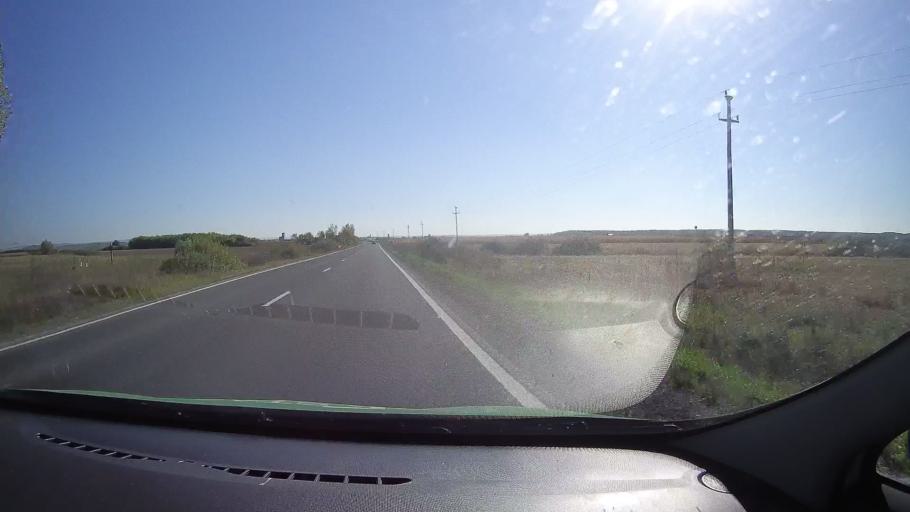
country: RO
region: Satu Mare
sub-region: Oras Ardud
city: Madaras
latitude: 47.6603
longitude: 22.8738
